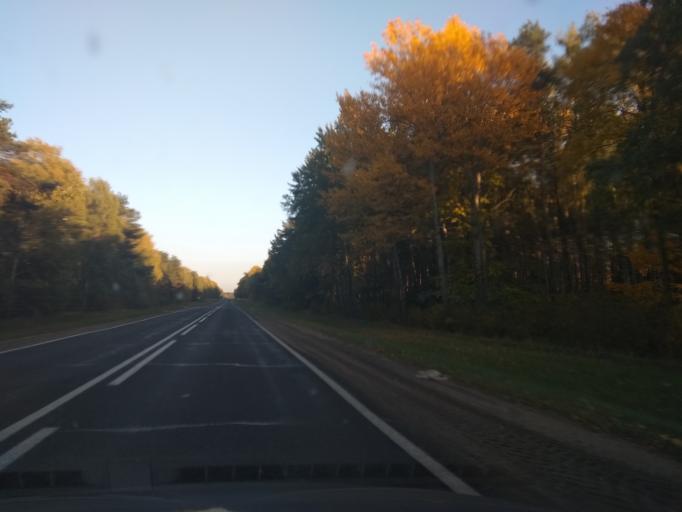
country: BY
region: Grodnenskaya
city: Vawkavysk
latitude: 53.1473
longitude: 24.5895
